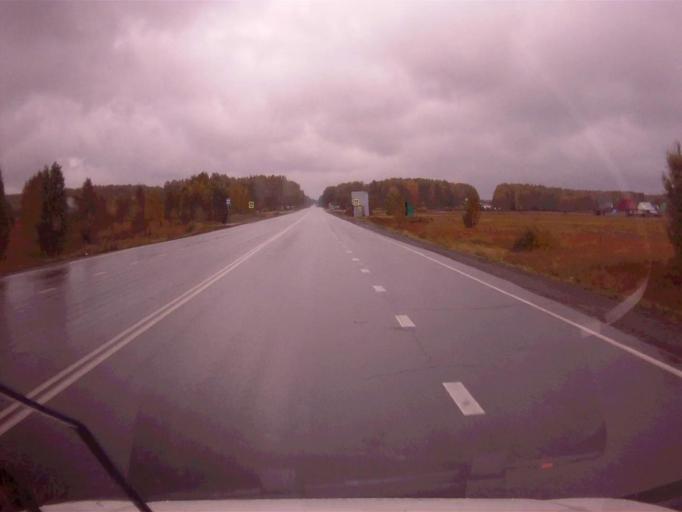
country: RU
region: Chelyabinsk
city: Argayash
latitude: 55.4561
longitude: 60.9277
